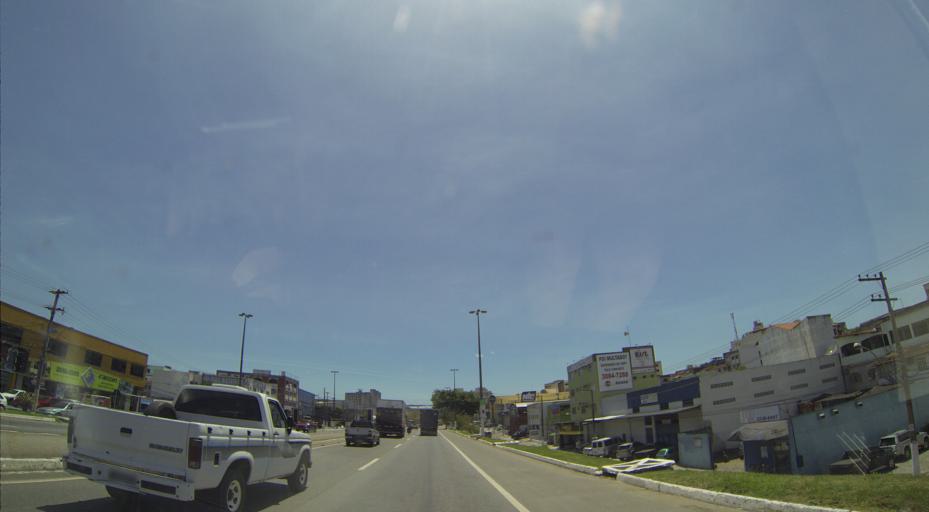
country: BR
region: Espirito Santo
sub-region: Vitoria
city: Vitoria
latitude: -20.3383
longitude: -40.3920
